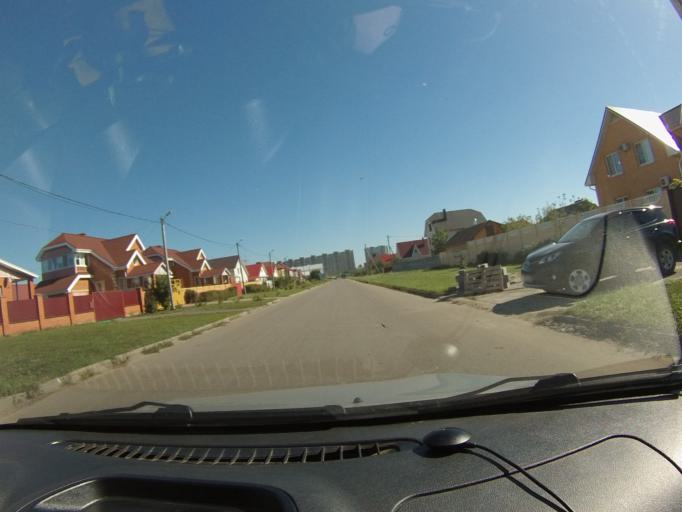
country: RU
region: Tambov
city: Tambov
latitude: 52.7692
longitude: 41.3853
